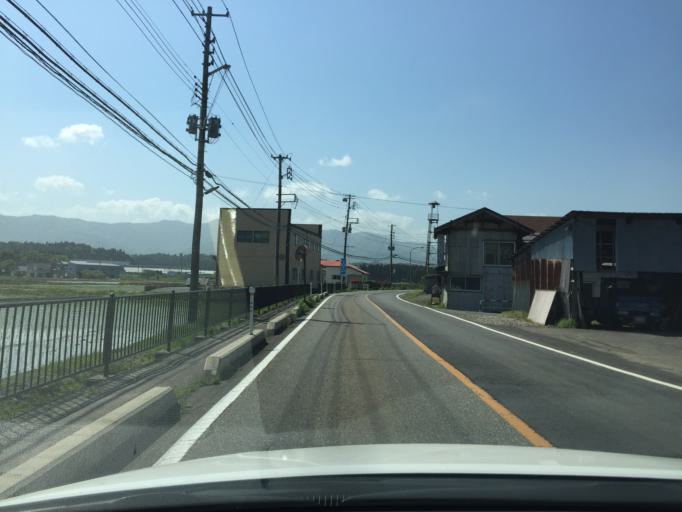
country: JP
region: Niigata
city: Muramatsu
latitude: 37.6846
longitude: 139.1520
